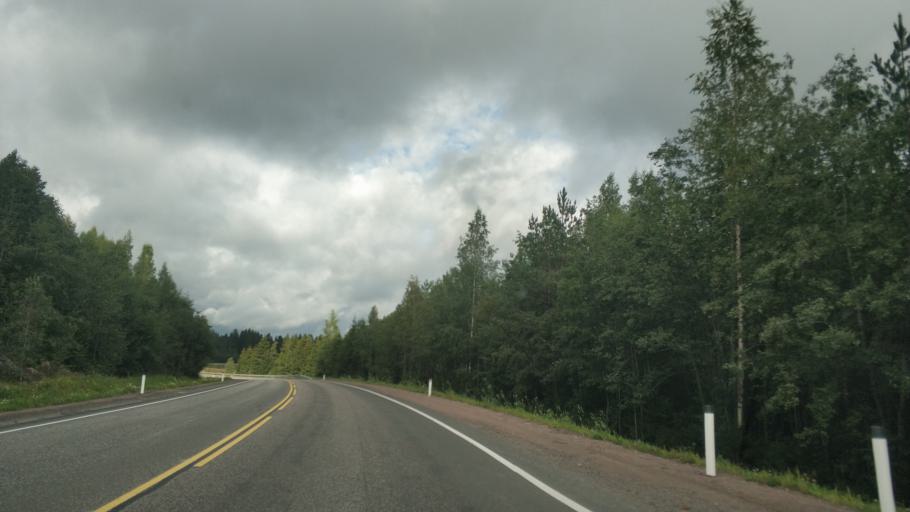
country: RU
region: Republic of Karelia
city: Khelyulya
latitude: 61.7849
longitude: 30.6524
